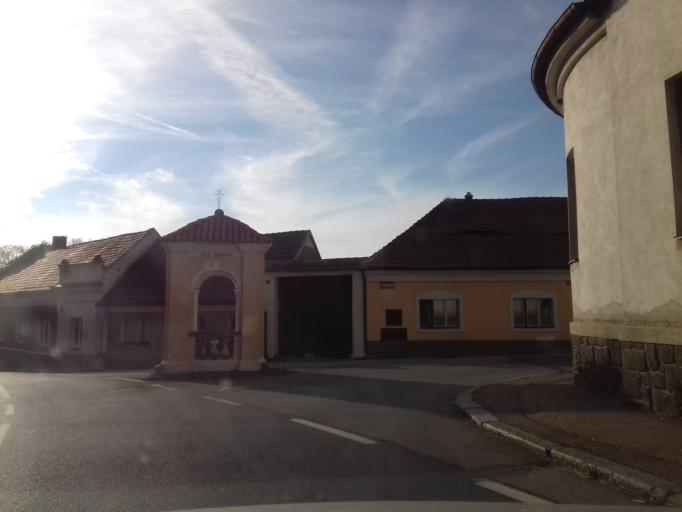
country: CZ
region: Central Bohemia
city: Neveklov
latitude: 49.7531
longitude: 14.5307
